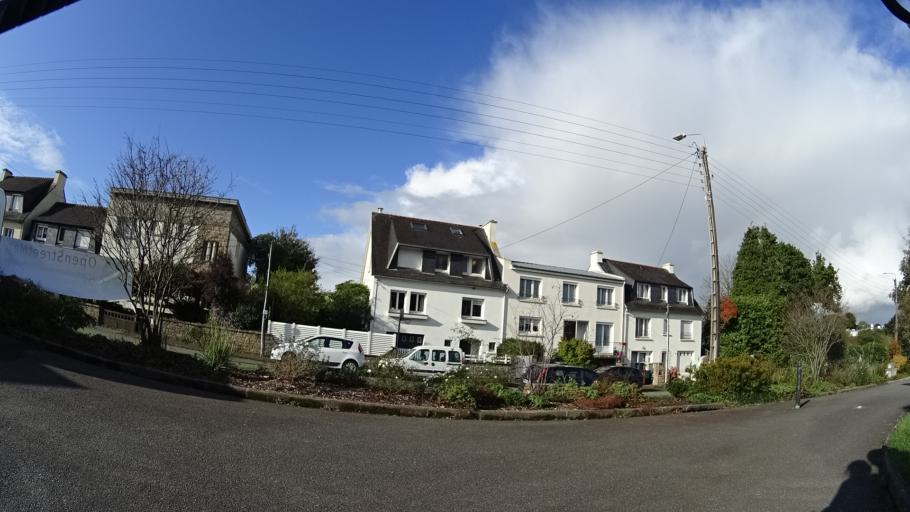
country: FR
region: Brittany
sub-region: Departement du Finistere
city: Brest
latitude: 48.4004
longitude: -4.4500
